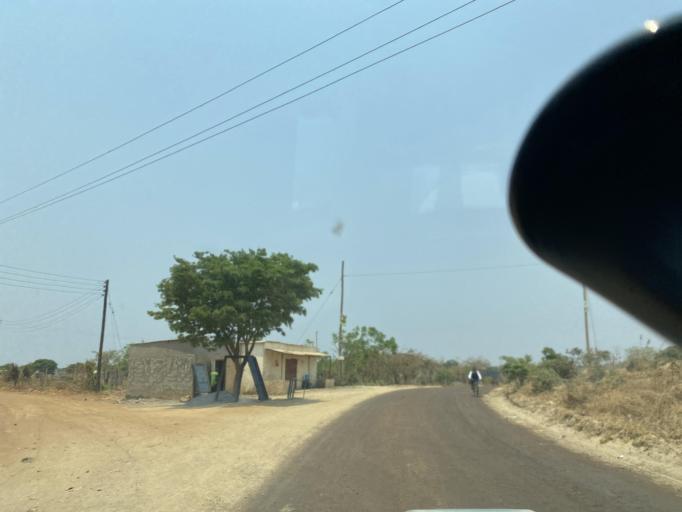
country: ZM
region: Lusaka
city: Lusaka
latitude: -15.5516
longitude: 28.3636
